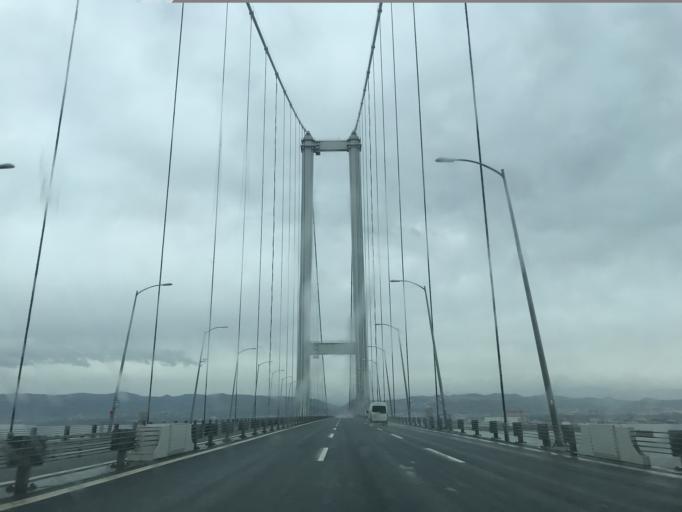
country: TR
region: Yalova
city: Altinova
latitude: 40.7513
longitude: 29.5151
